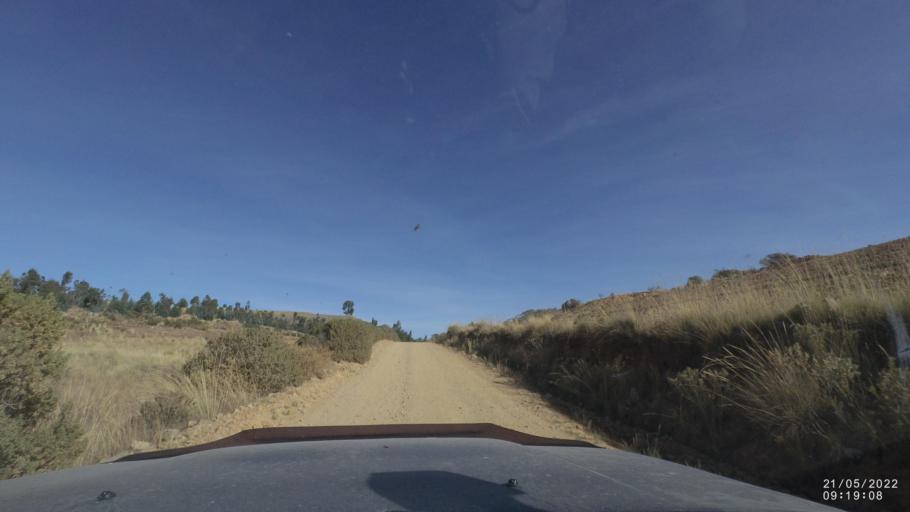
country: BO
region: Cochabamba
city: Cochabamba
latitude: -17.3582
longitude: -66.0187
